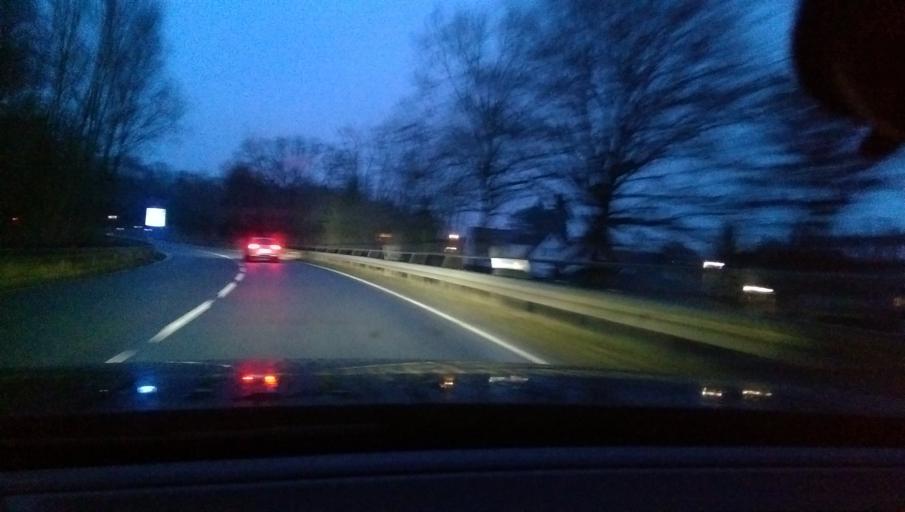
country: DE
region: Lower Saxony
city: Gross Munzel
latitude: 52.4091
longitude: 9.5185
